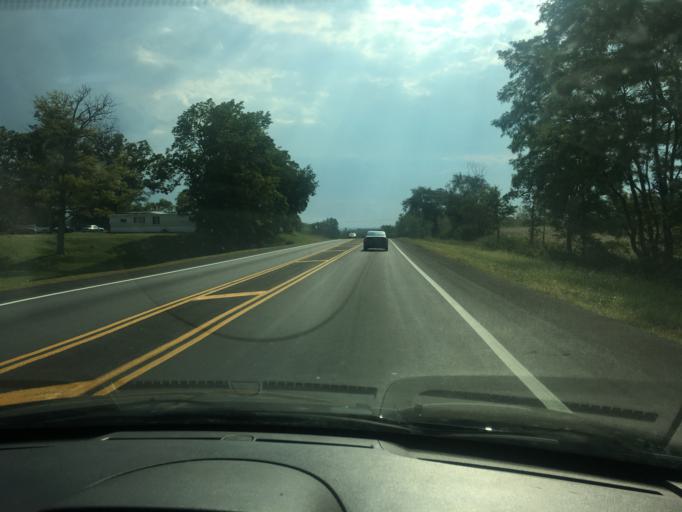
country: US
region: Ohio
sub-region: Champaign County
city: Urbana
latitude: 40.0707
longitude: -83.7708
